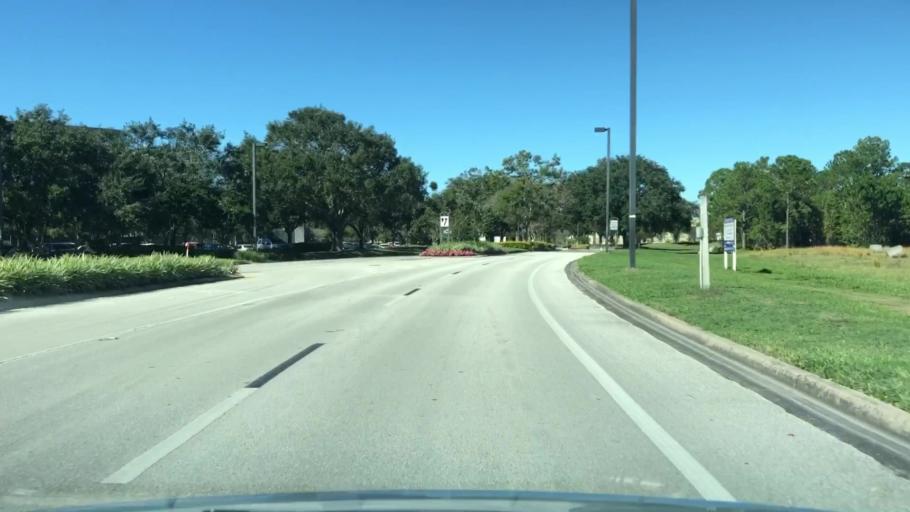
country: US
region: Florida
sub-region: Orange County
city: Conway
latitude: 28.4599
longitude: -81.3015
